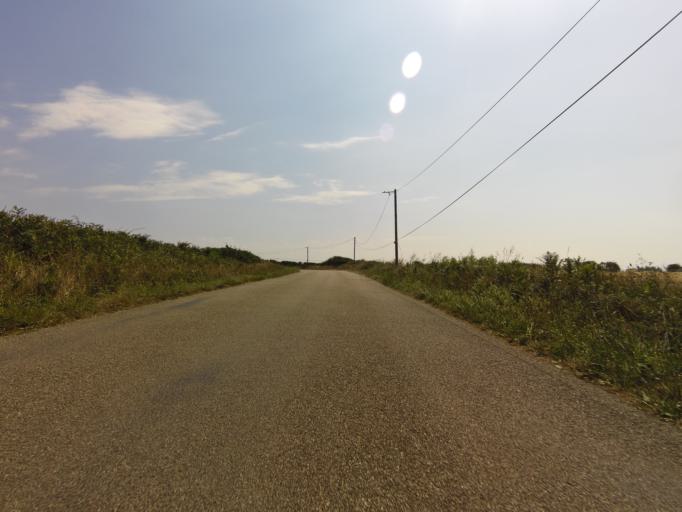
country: FR
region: Brittany
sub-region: Departement du Finistere
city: Pouldreuzic
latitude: 47.9110
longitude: -4.3419
